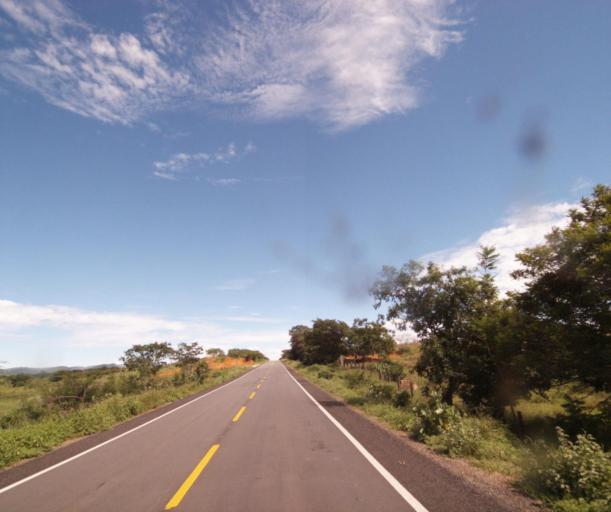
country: BR
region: Bahia
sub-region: Guanambi
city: Guanambi
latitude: -14.3856
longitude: -42.7643
